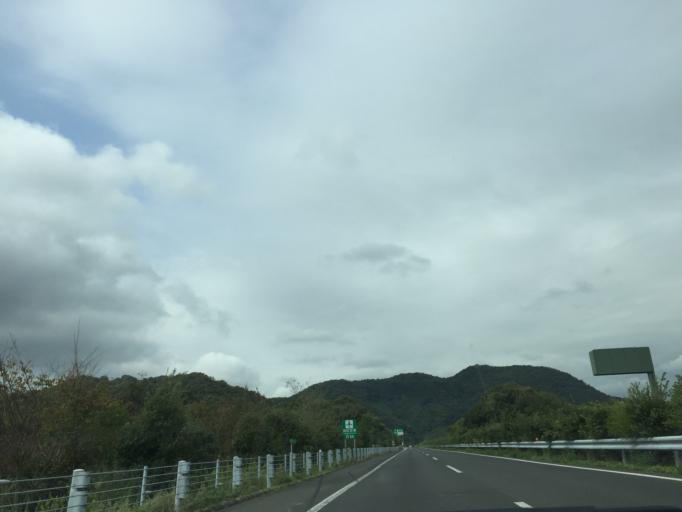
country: JP
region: Kagawa
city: Shido
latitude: 34.2762
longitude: 134.2721
